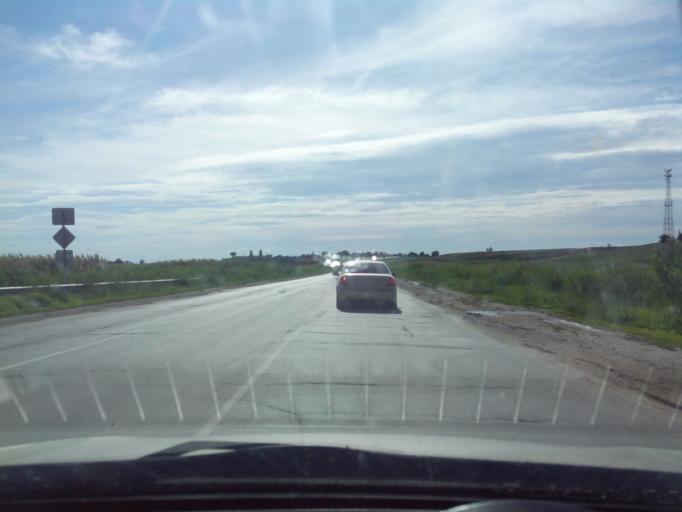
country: RU
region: Astrakhan
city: Znamensk
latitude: 48.5755
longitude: 45.7292
